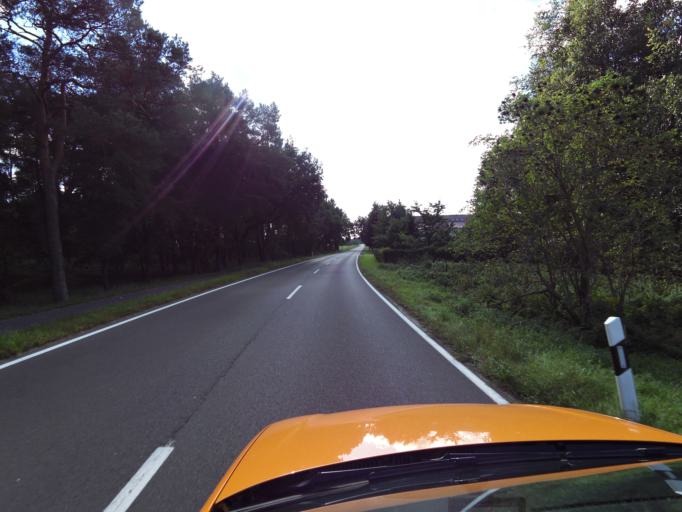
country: DE
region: Brandenburg
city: Michendorf
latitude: 52.2835
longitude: 13.0685
